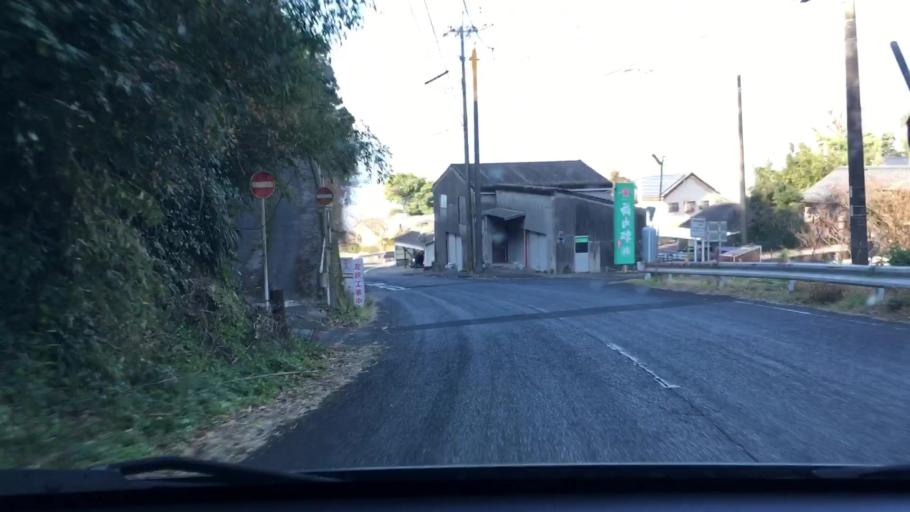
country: JP
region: Kagoshima
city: Kokubu-matsuki
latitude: 31.6702
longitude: 130.8207
